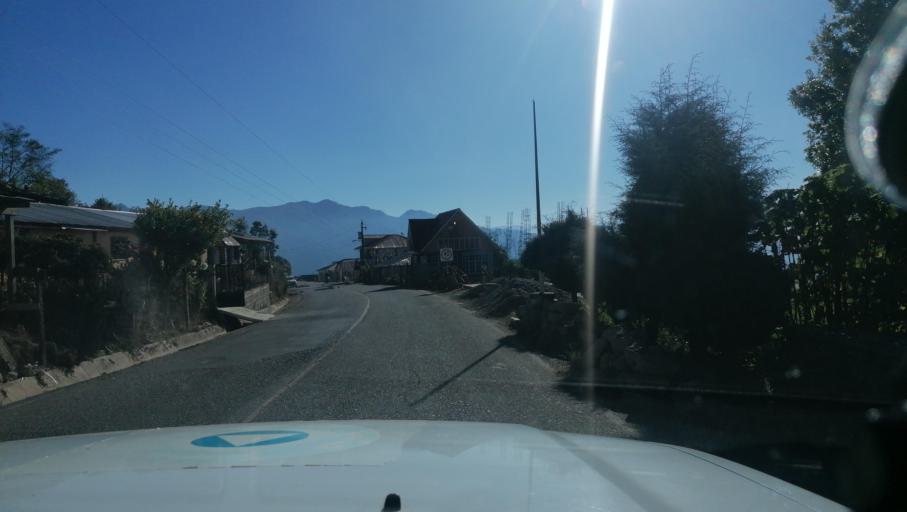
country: MX
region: Chiapas
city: Motozintla de Mendoza
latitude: 15.2379
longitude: -92.2328
